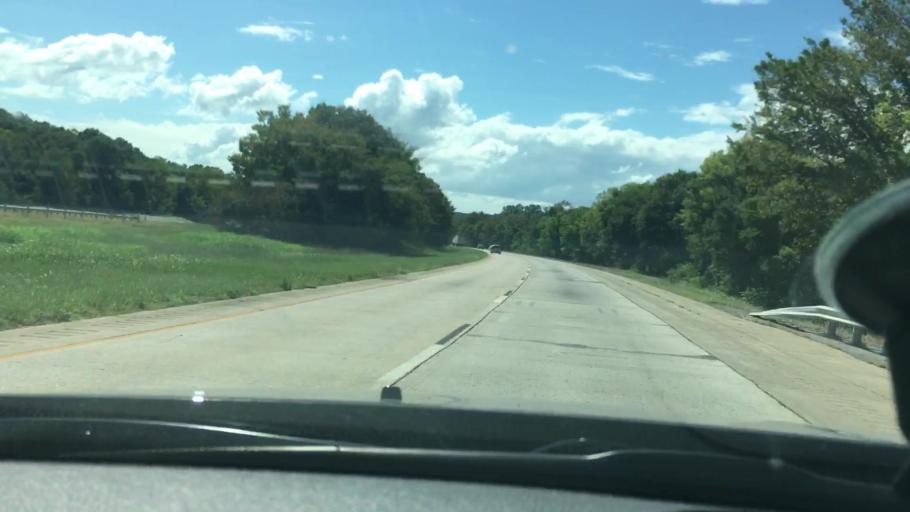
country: US
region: Oklahoma
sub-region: Sequoyah County
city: Vian
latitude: 35.4935
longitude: -95.0084
